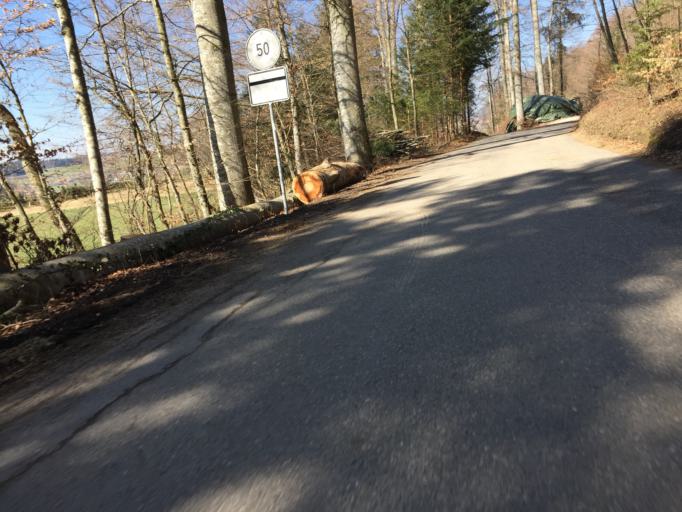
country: CH
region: Bern
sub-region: Bern-Mittelland District
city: Worb
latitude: 46.9091
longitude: 7.5788
